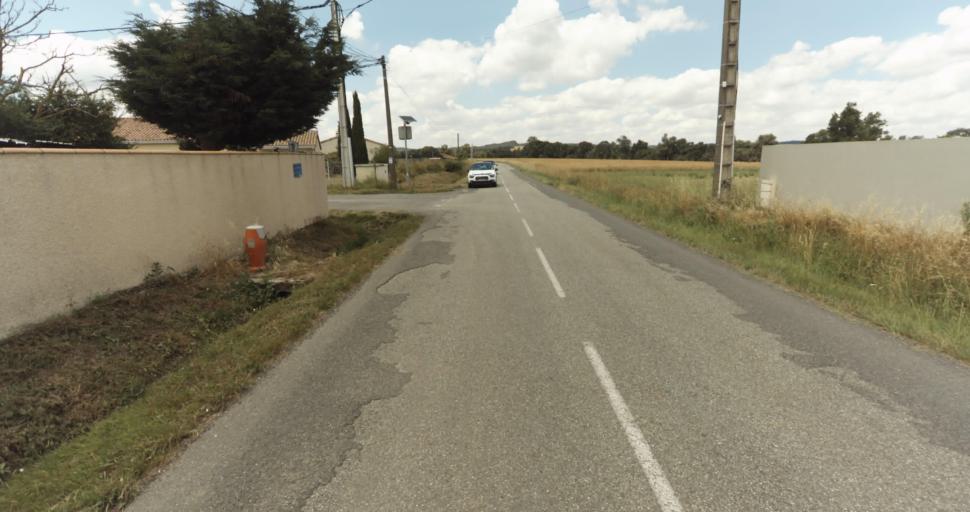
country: FR
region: Midi-Pyrenees
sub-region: Departement de la Haute-Garonne
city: Fontenilles
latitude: 43.5467
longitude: 1.1817
